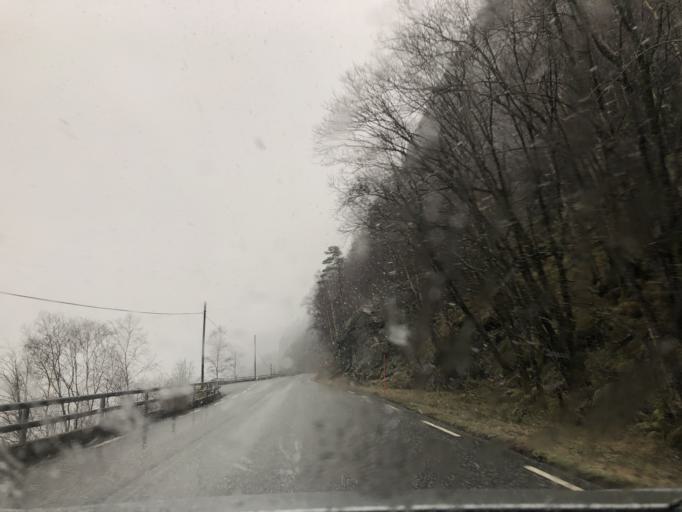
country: NO
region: Rogaland
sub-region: Suldal
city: Sand
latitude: 59.4107
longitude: 6.2145
